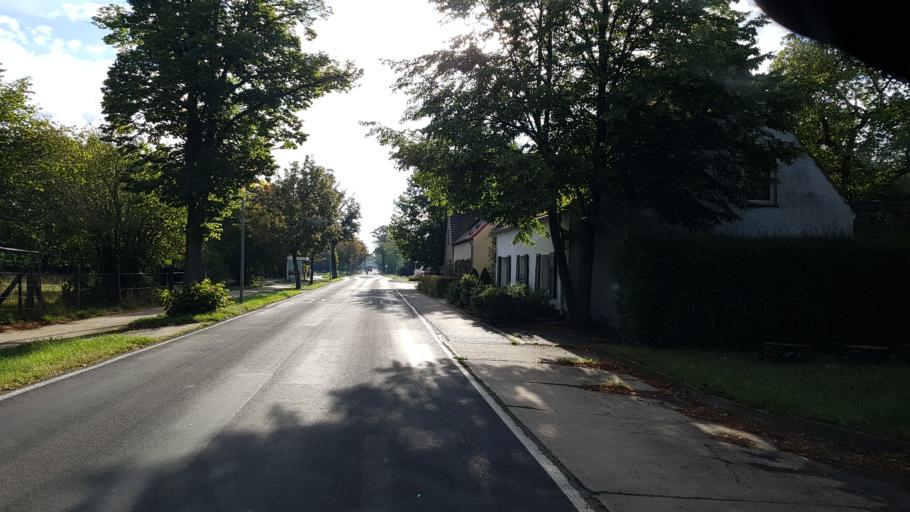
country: DE
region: Brandenburg
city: Welzow
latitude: 51.5508
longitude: 14.2050
